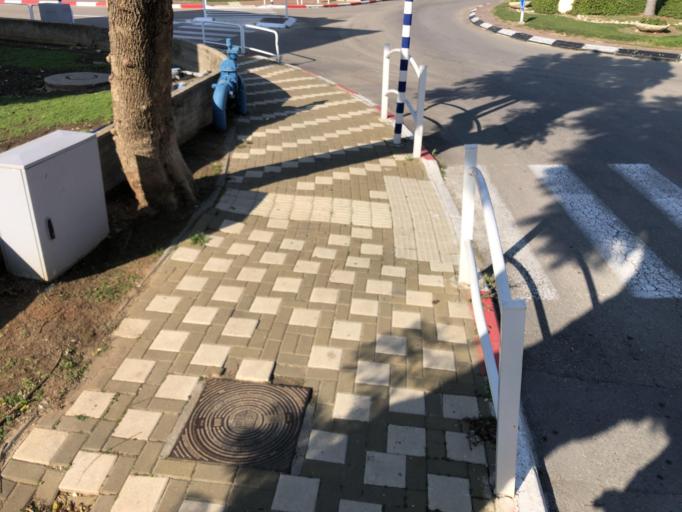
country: IL
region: Northern District
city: `Akko
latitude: 32.9201
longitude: 35.0918
